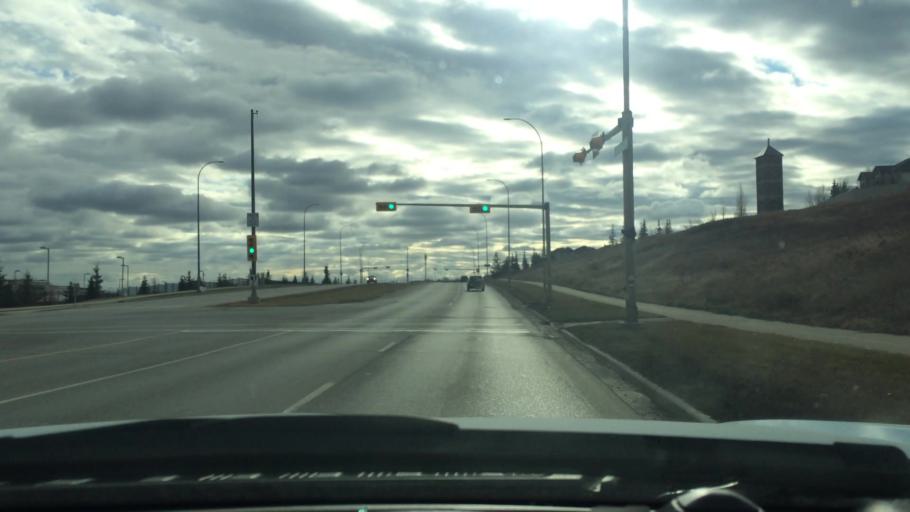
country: CA
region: Alberta
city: Calgary
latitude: 51.1634
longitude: -114.1282
